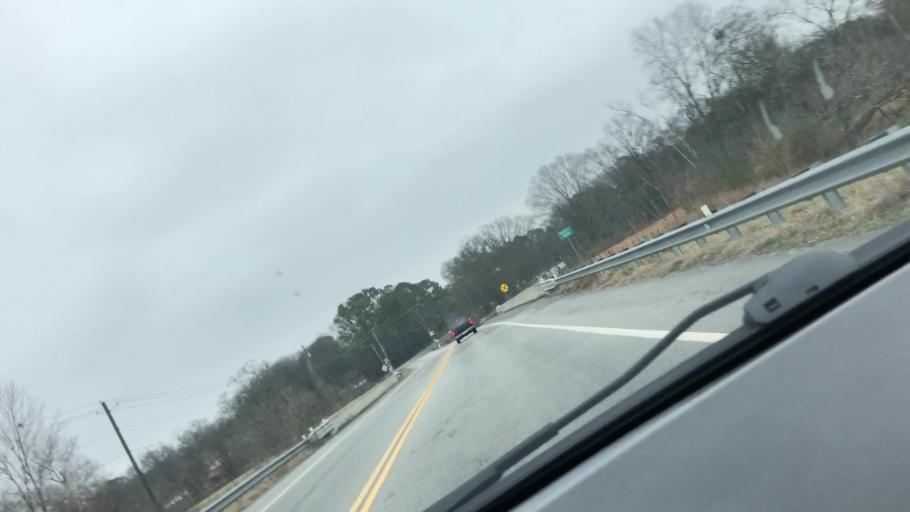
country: US
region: Georgia
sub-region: Bartow County
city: Cartersville
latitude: 34.1990
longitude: -84.8344
